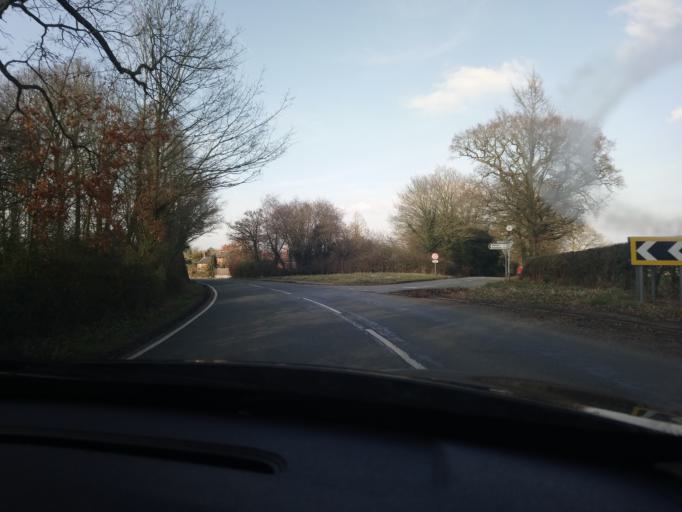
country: GB
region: England
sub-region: Shropshire
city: Bicton
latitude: 52.7523
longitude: -2.7794
